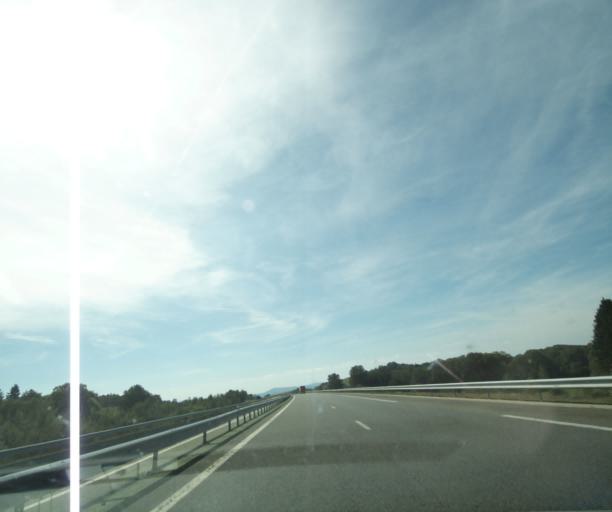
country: FR
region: Auvergne
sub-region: Departement du Puy-de-Dome
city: Saint-Ours
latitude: 45.8776
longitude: 2.9092
